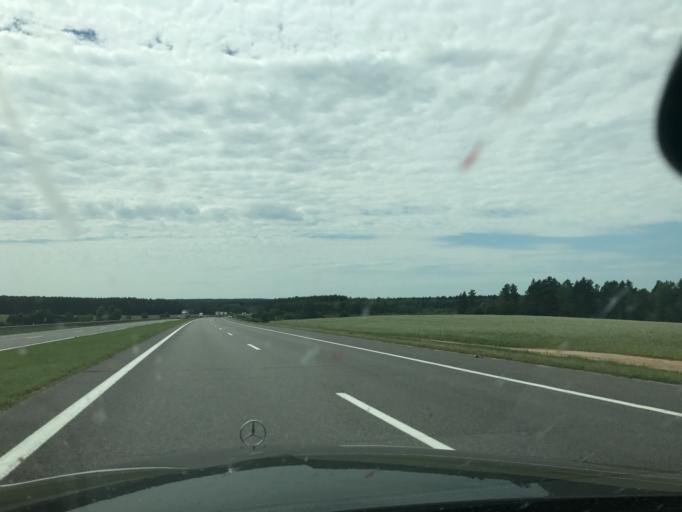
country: BY
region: Minsk
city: Zamostochcha
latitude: 53.8831
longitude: 27.9365
